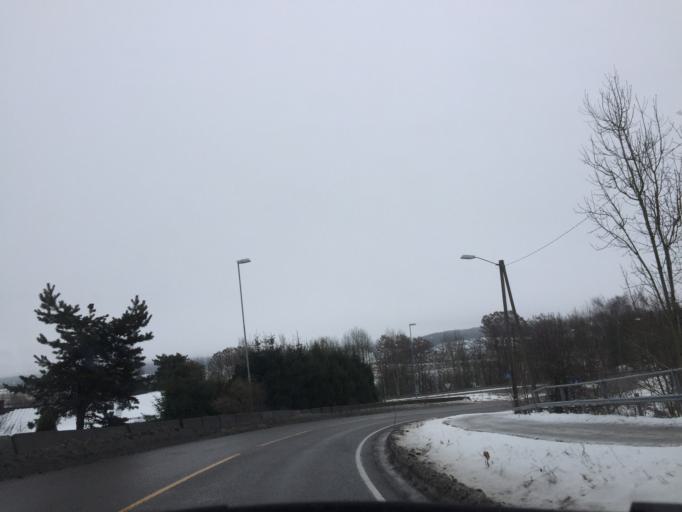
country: NO
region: Akershus
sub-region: Frogn
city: Drobak
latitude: 59.6863
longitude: 10.6675
